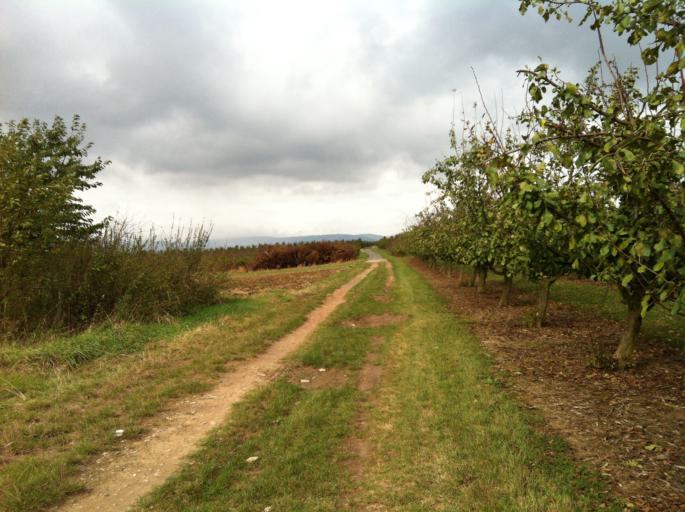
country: DE
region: Rheinland-Pfalz
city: Ober-Olm
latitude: 49.9685
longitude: 8.1710
